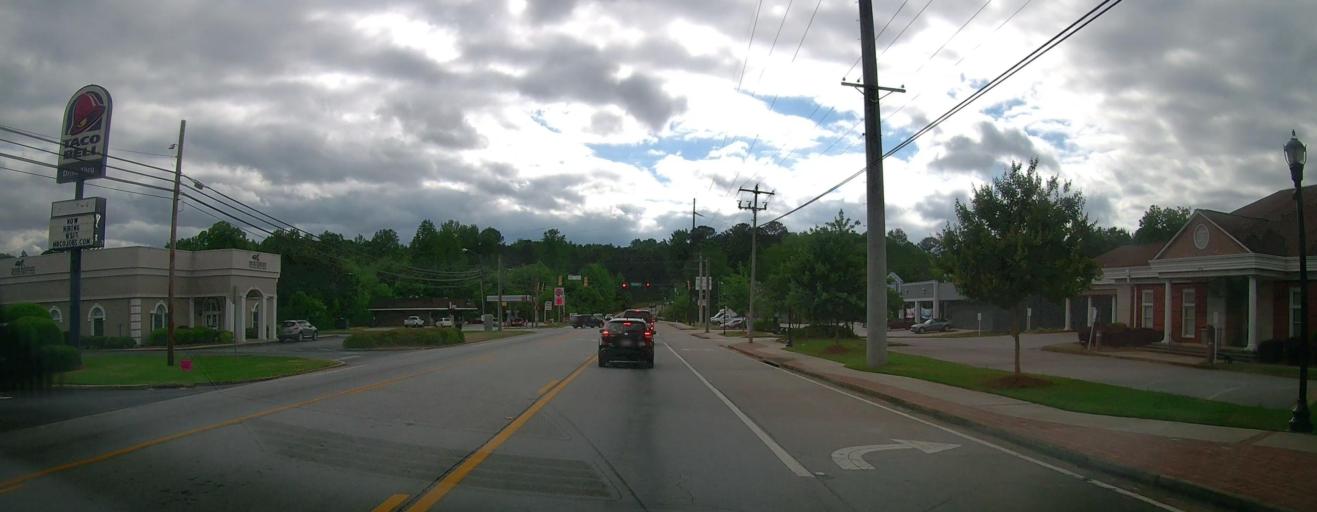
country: US
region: Georgia
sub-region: Walton County
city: Monroe
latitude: 33.7924
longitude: -83.7340
